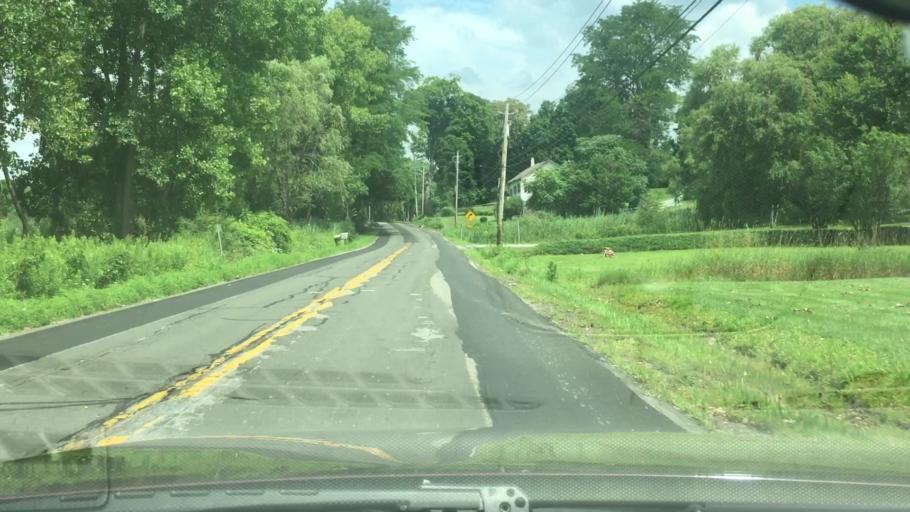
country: US
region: New York
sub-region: Dutchess County
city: Pawling
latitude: 41.6006
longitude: -73.6829
